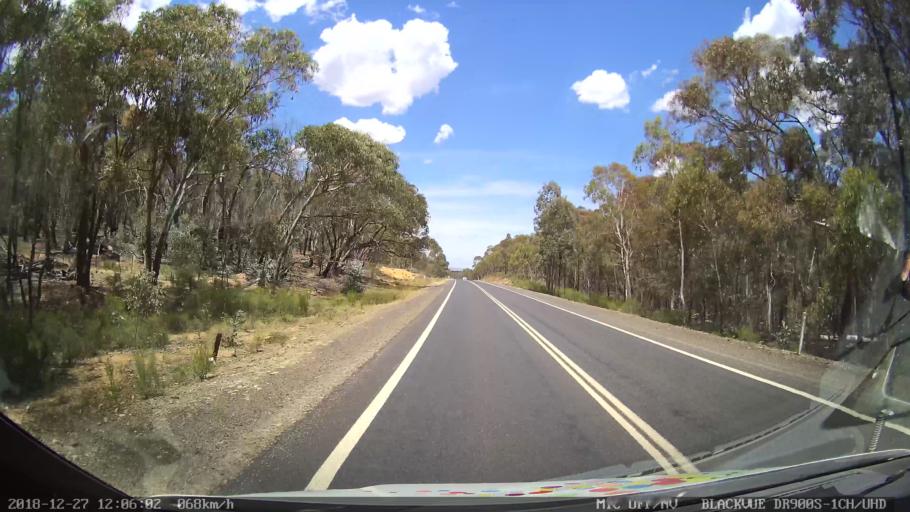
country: AU
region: New South Wales
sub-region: Blayney
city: Blayney
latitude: -33.8053
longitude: 149.3322
